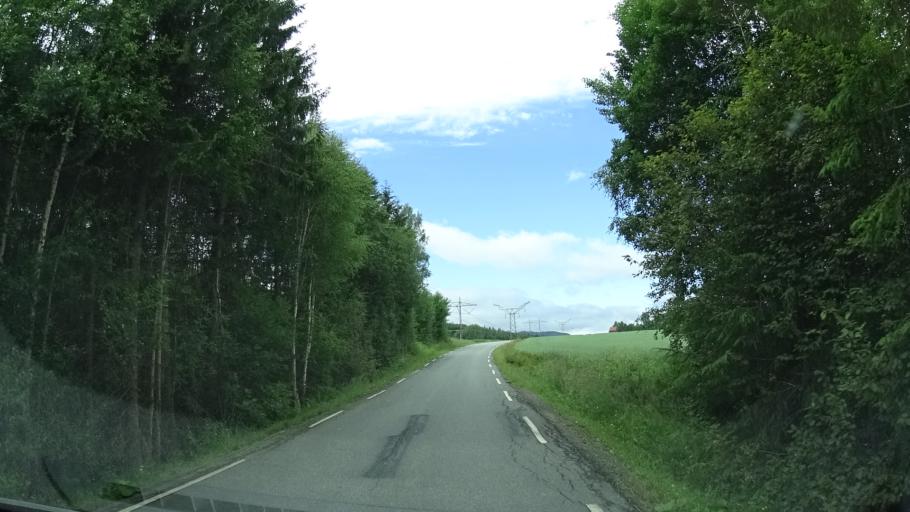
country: NO
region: Buskerud
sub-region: Ringerike
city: Honefoss
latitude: 60.2031
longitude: 10.0649
